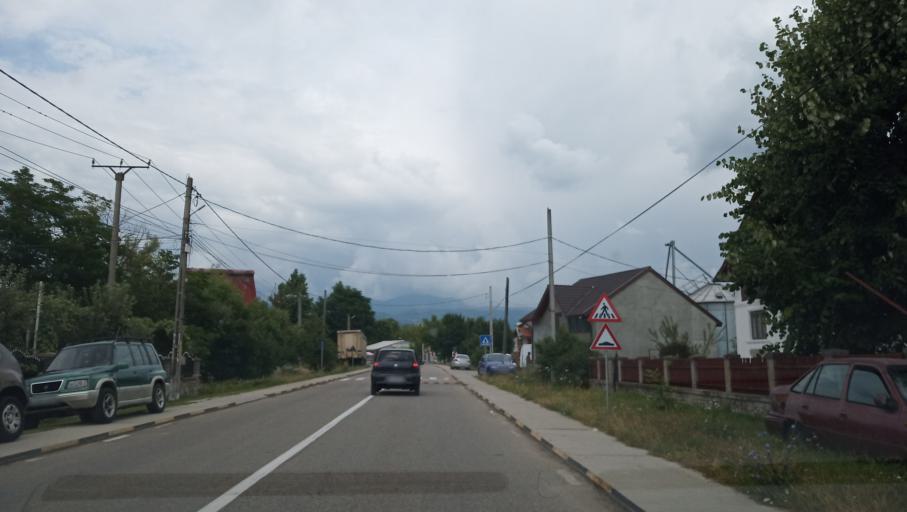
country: RO
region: Gorj
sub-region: Comuna Tismana
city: Tismana
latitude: 45.0419
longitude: 22.9520
